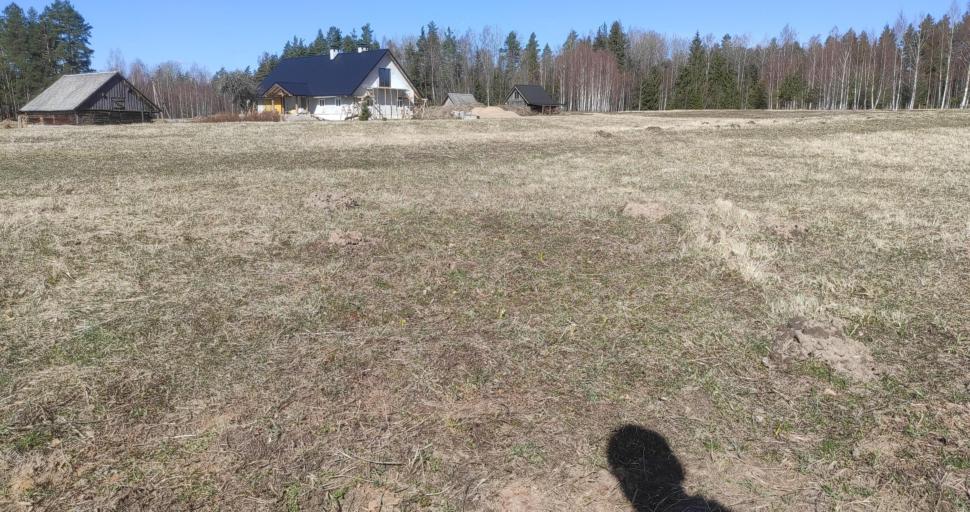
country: LV
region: Kuldigas Rajons
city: Kuldiga
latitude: 57.0532
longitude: 21.9591
